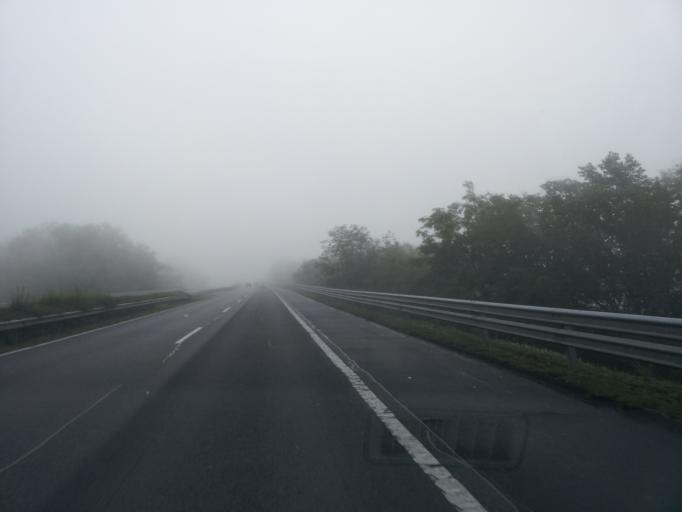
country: HU
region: Pest
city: Hevizgyoerk
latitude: 47.6415
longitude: 19.5172
